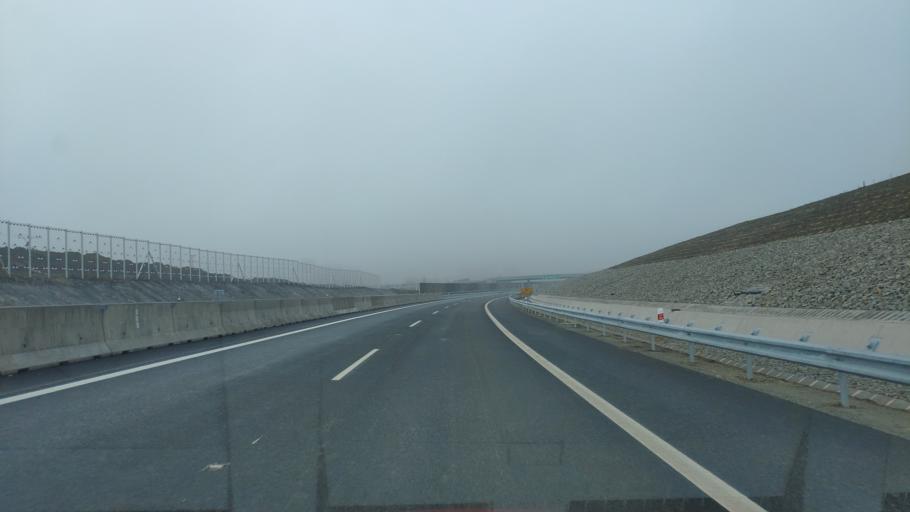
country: SK
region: Kosicky
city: Kosice
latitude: 48.7410
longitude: 21.3519
